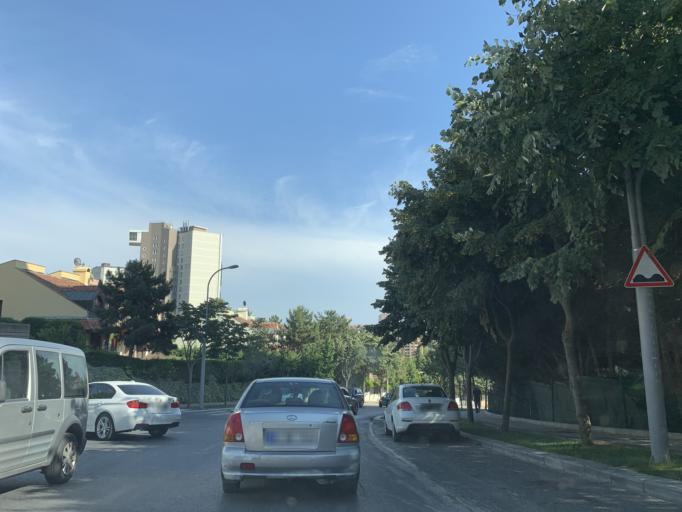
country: TR
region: Istanbul
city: Esenyurt
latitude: 41.0720
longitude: 28.6841
